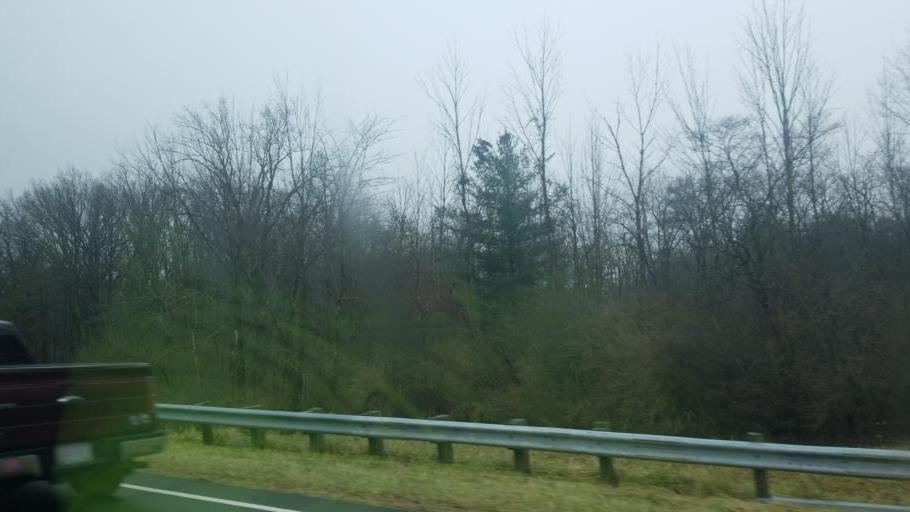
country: US
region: Ohio
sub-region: Union County
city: Marysville
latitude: 40.2462
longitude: -83.4083
